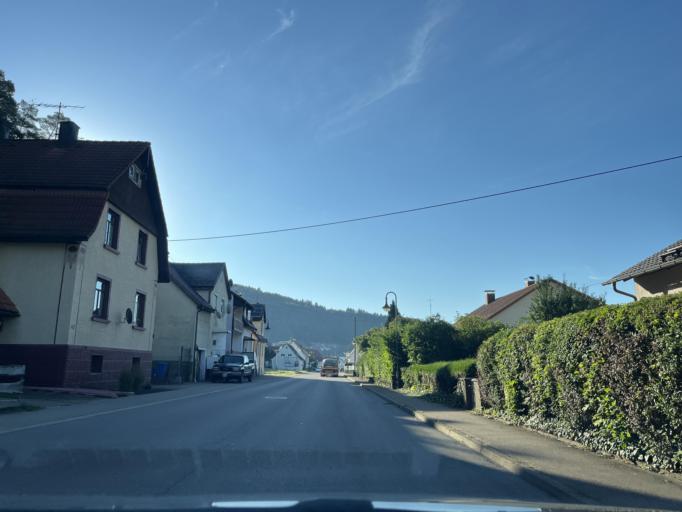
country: DE
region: Baden-Wuerttemberg
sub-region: Tuebingen Region
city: Neufra
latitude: 48.2778
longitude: 9.1632
